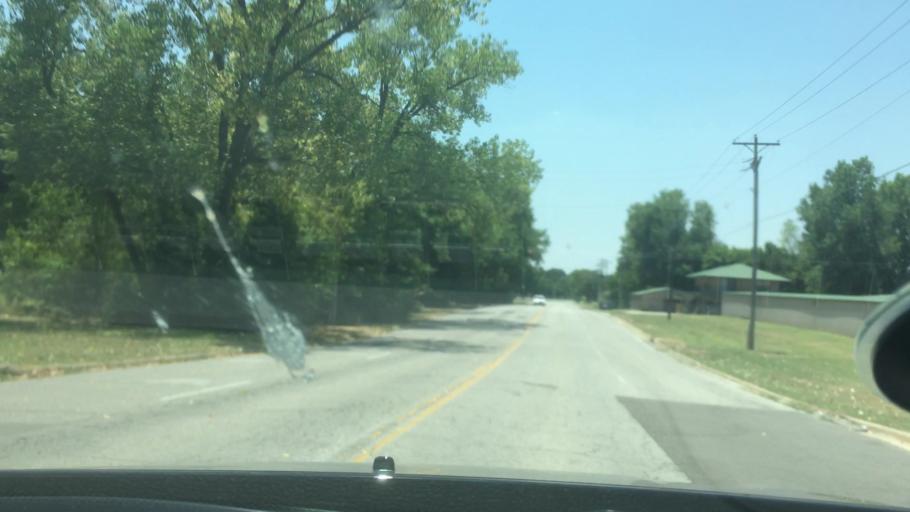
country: US
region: Oklahoma
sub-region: Pontotoc County
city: Ada
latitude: 34.7632
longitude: -96.6612
